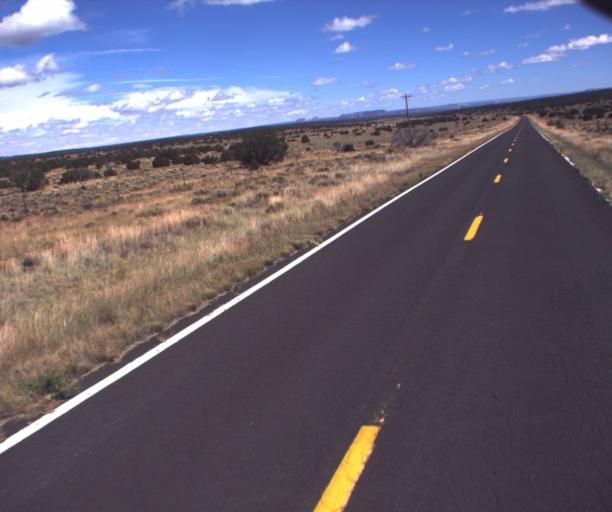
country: US
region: New Mexico
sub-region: McKinley County
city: Zuni Pueblo
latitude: 34.9894
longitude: -109.1116
